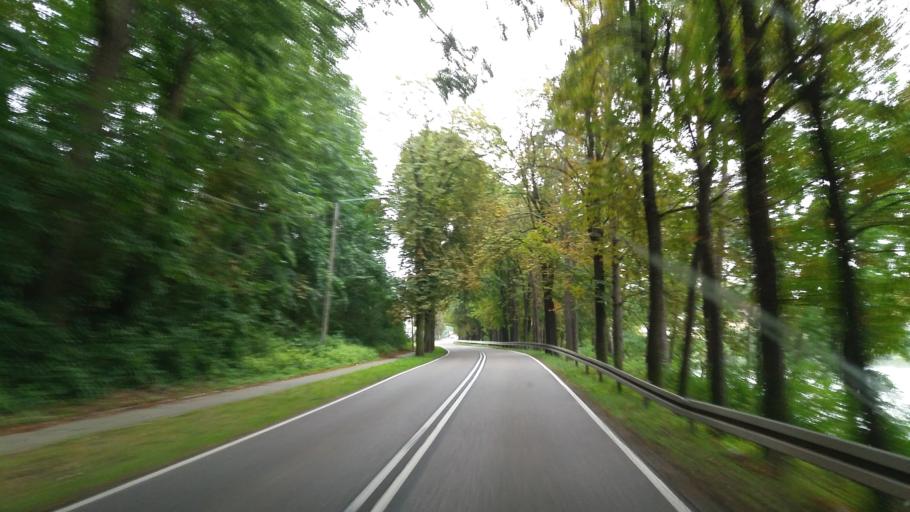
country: PL
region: West Pomeranian Voivodeship
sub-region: Powiat mysliborski
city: Barlinek
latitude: 53.0004
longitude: 15.2240
